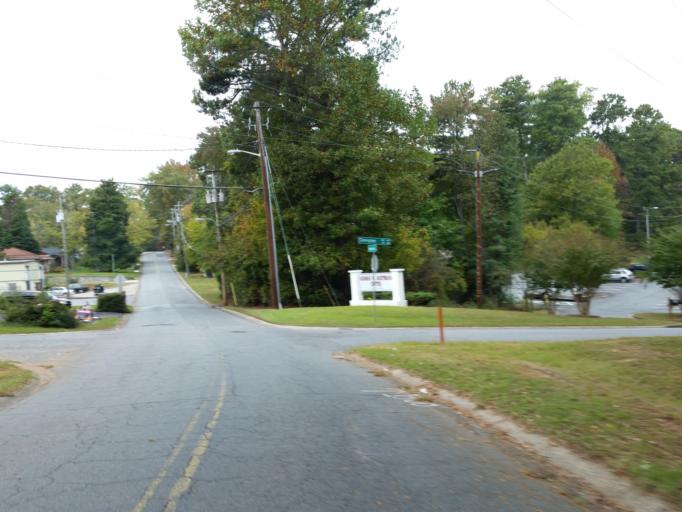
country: US
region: Georgia
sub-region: Cobb County
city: Marietta
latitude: 33.9530
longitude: -84.5295
